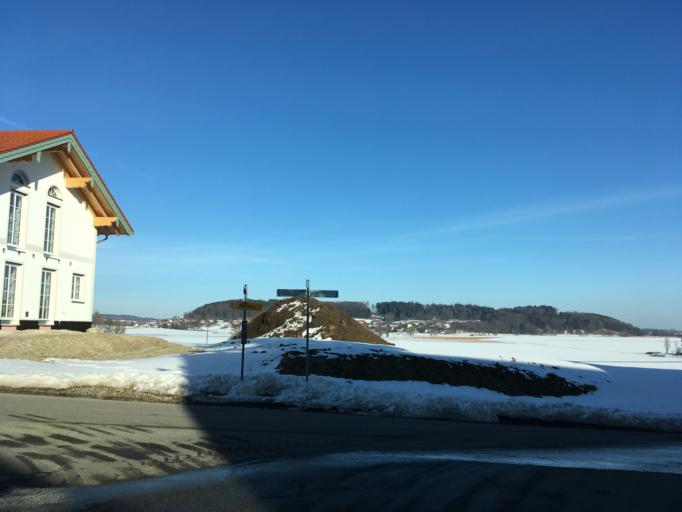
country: DE
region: Bavaria
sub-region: Upper Bavaria
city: Steinhoring
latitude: 48.0980
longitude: 12.0197
